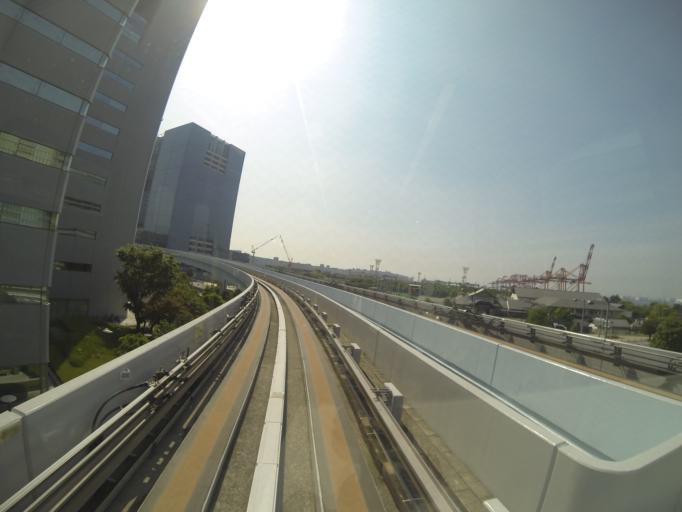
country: JP
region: Tokyo
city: Tokyo
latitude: 35.6173
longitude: 139.7766
